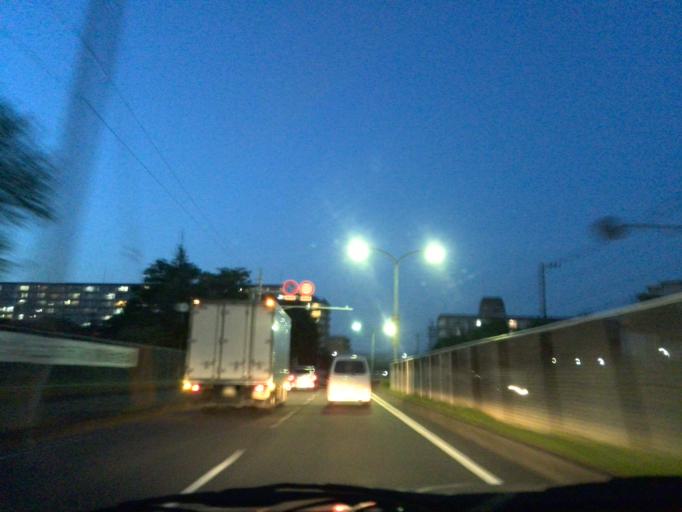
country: JP
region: Chiba
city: Funabashi
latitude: 35.6750
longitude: 140.0119
